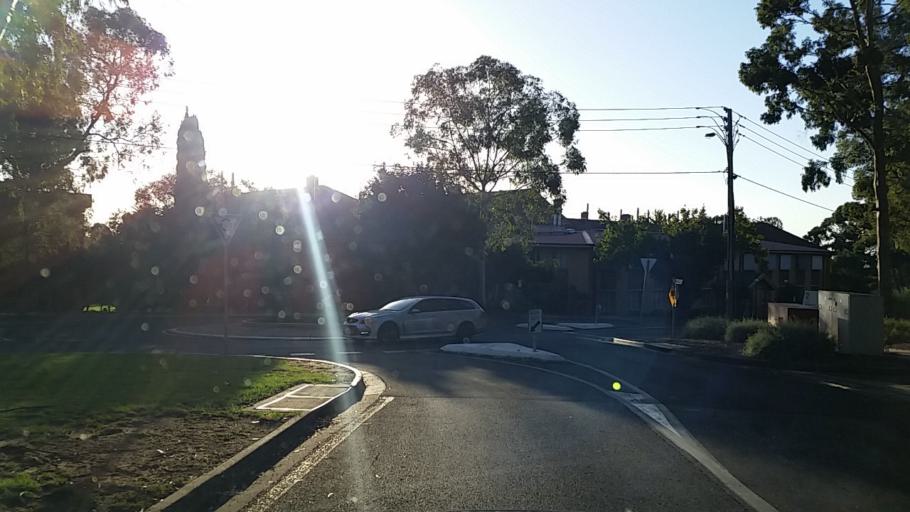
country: AU
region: South Australia
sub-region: Mitcham
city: Mitcham
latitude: -34.9686
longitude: 138.6362
